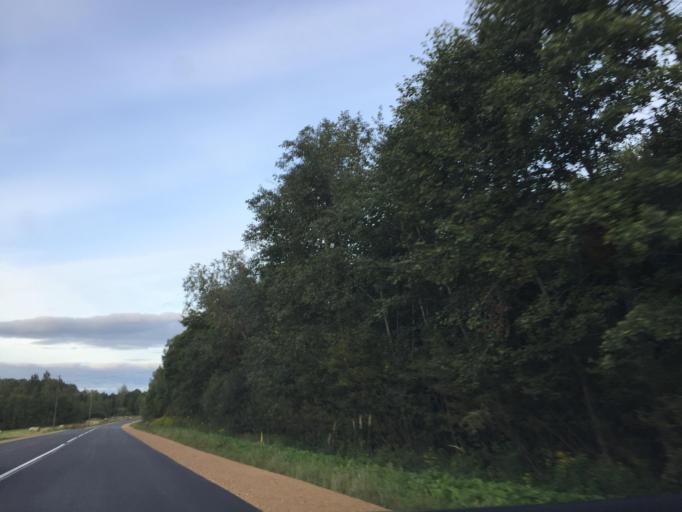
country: LV
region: Viesite
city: Viesite
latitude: 56.3902
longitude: 25.6767
